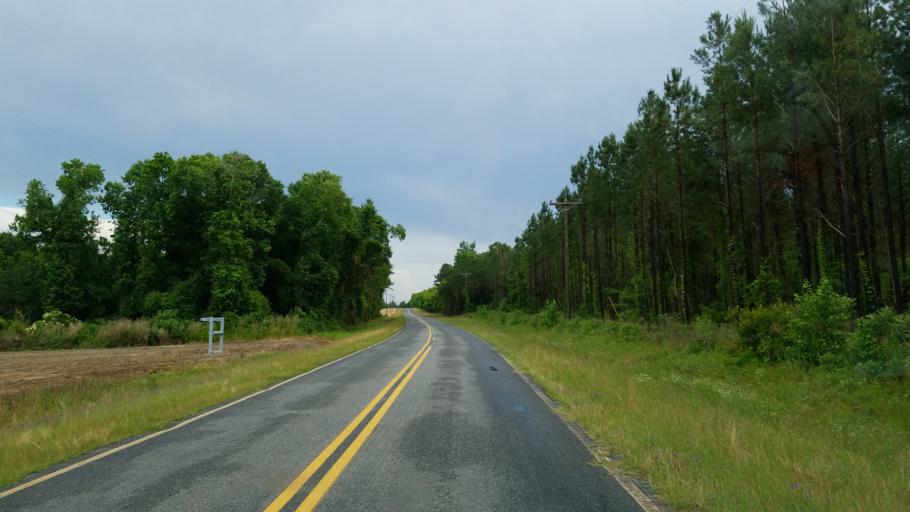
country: US
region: Georgia
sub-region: Dooly County
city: Unadilla
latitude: 32.2056
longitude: -83.7982
